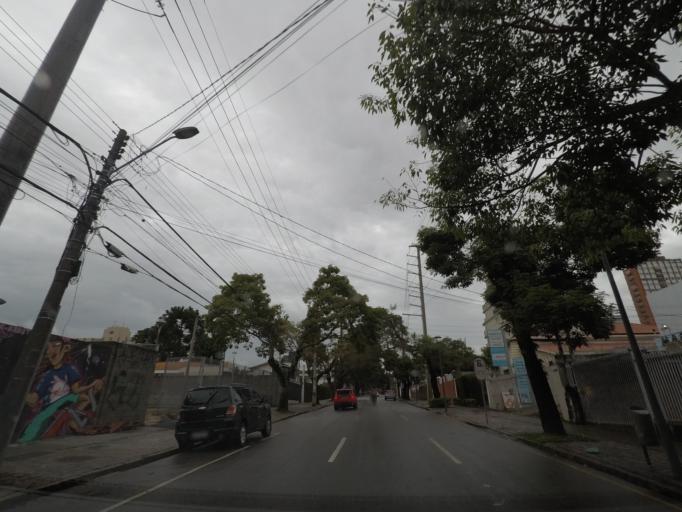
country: BR
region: Parana
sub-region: Curitiba
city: Curitiba
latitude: -25.4486
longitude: -49.2802
